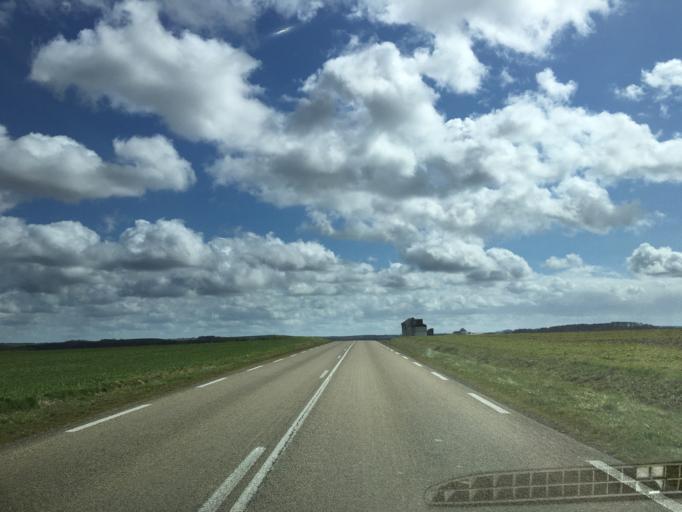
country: FR
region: Bourgogne
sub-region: Departement de l'Yonne
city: Aillant-sur-Tholon
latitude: 47.8543
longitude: 3.3747
